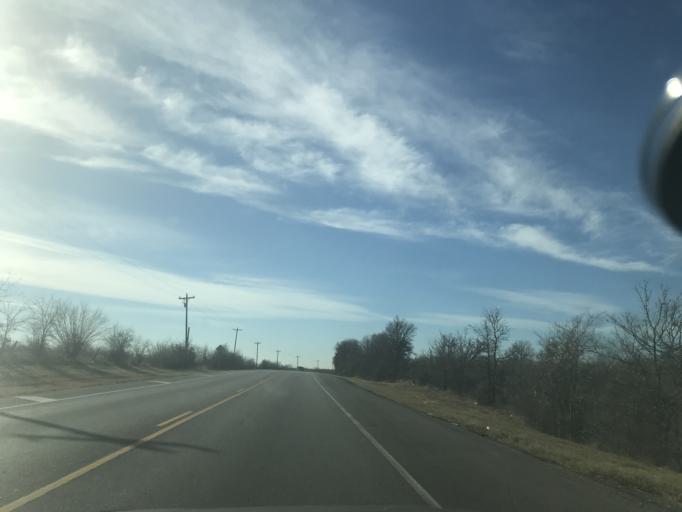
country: US
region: Texas
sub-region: Travis County
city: Manor
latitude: 30.3253
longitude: -97.5611
